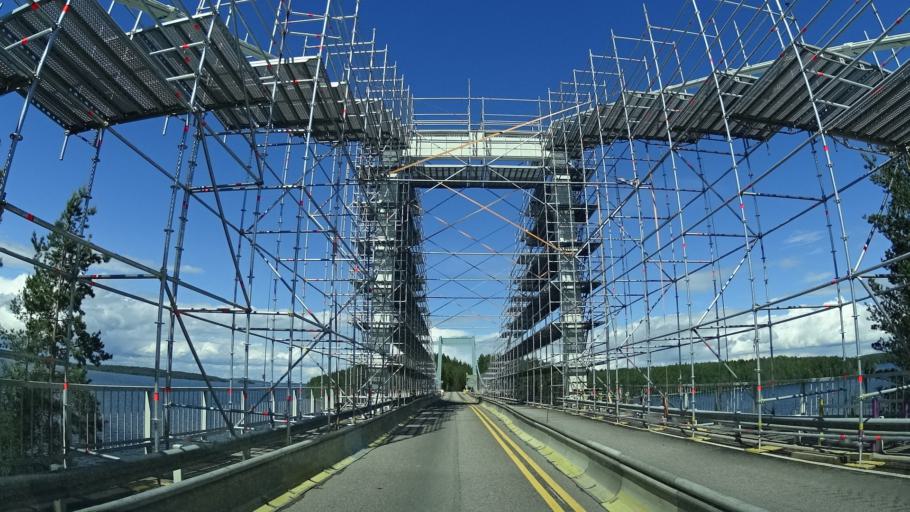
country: FI
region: Paijanne Tavastia
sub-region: Lahti
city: Asikkala
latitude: 61.2922
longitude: 25.5324
